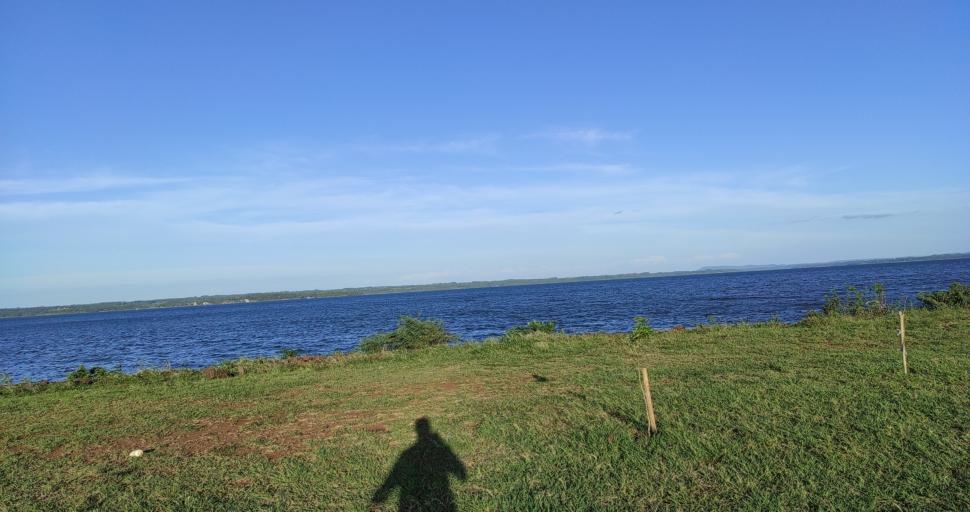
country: AR
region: Misiones
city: Garupa
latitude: -27.4307
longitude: -55.8626
